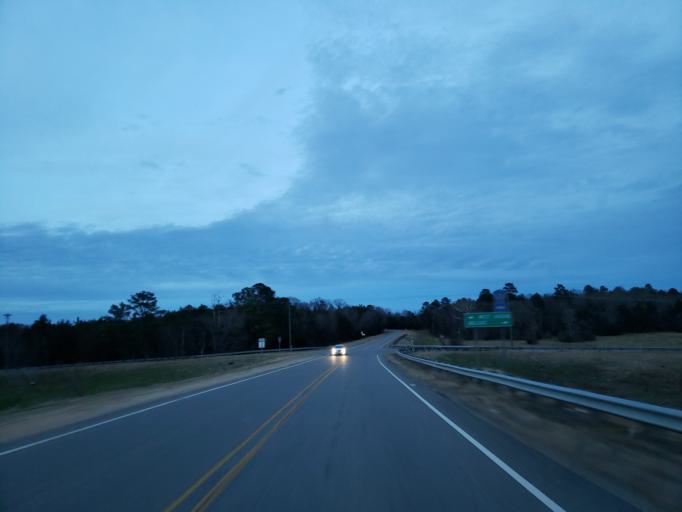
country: US
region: Alabama
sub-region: Greene County
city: Eutaw
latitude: 32.8593
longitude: -88.0987
